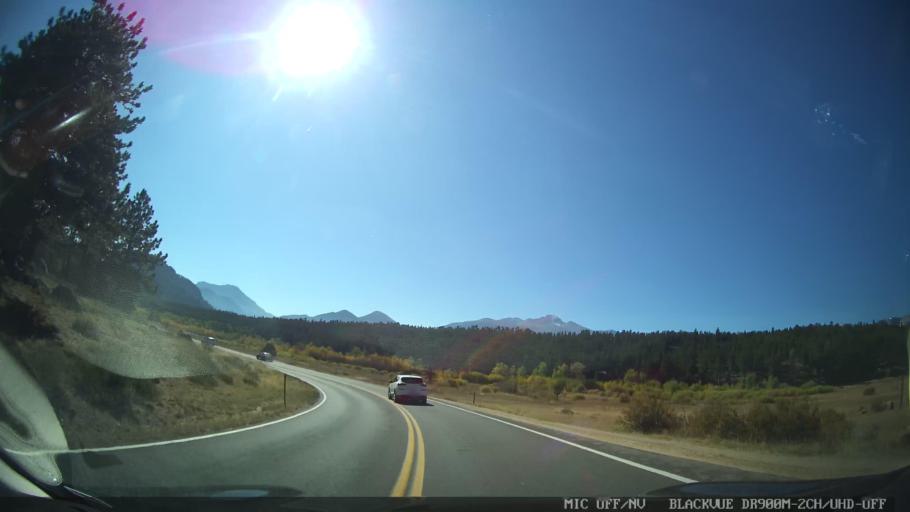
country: US
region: Colorado
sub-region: Larimer County
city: Estes Park
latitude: 40.3691
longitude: -105.5929
